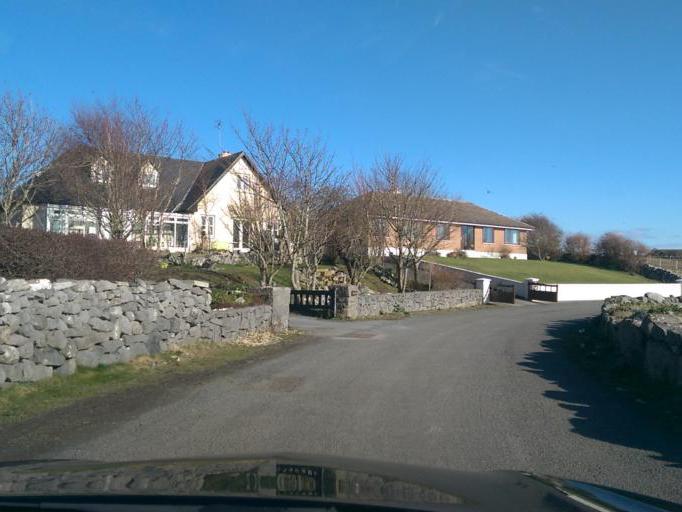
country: IE
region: Connaught
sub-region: County Galway
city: Oranmore
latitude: 53.2408
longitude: -8.9610
